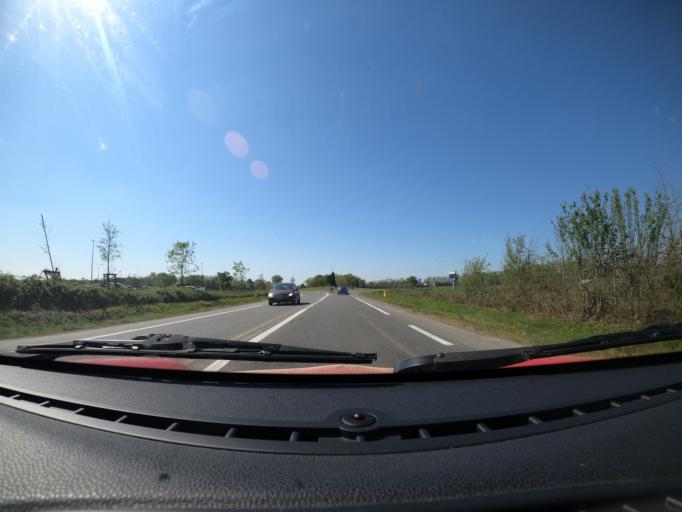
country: FR
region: Aquitaine
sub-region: Departement des Pyrenees-Atlantiques
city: Lescar
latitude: 43.3450
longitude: -0.4214
